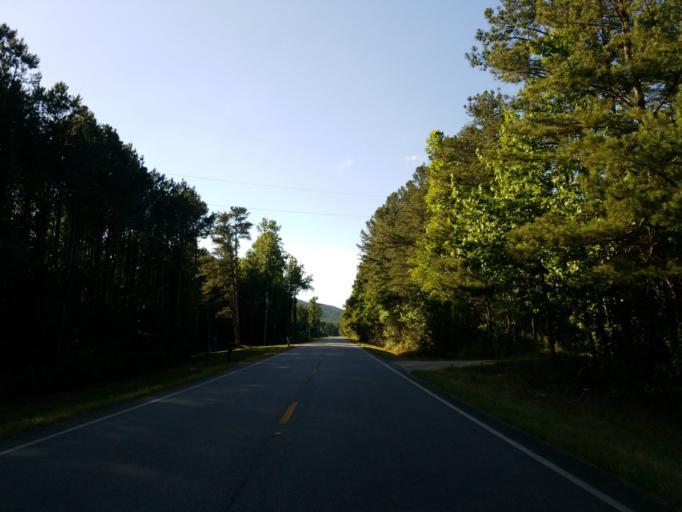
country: US
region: Georgia
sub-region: Gordon County
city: Calhoun
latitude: 34.6155
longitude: -85.0513
